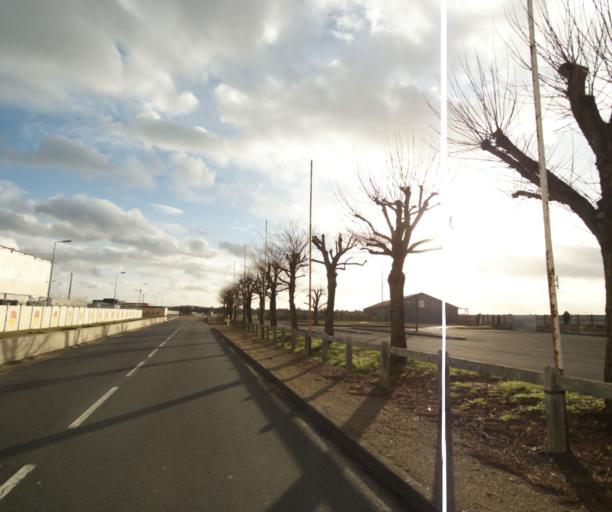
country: FR
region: Pays de la Loire
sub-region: Departement de la Sarthe
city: Arnage
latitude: 47.9507
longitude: 0.2066
